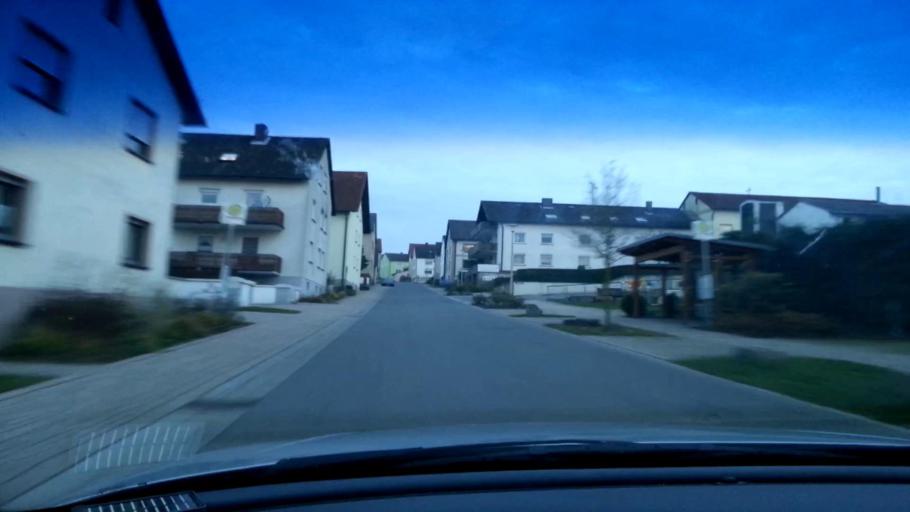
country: DE
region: Bavaria
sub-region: Upper Franconia
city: Breitengussbach
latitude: 49.9790
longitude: 10.8963
